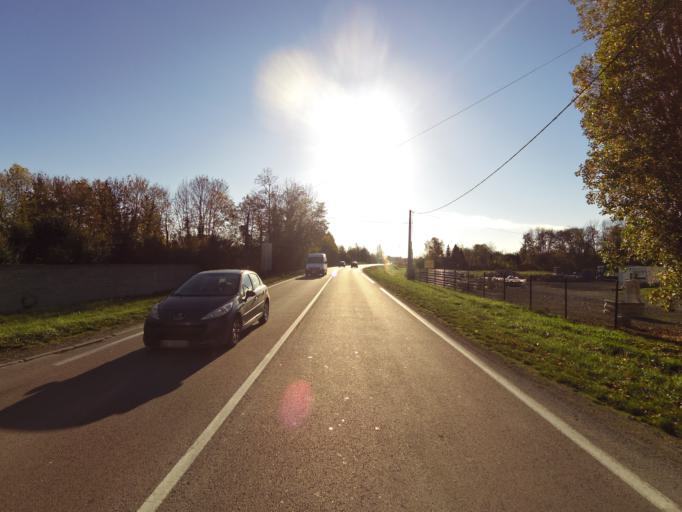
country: FR
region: Champagne-Ardenne
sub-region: Departement de l'Aube
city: Bucheres
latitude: 48.2292
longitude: 4.1290
